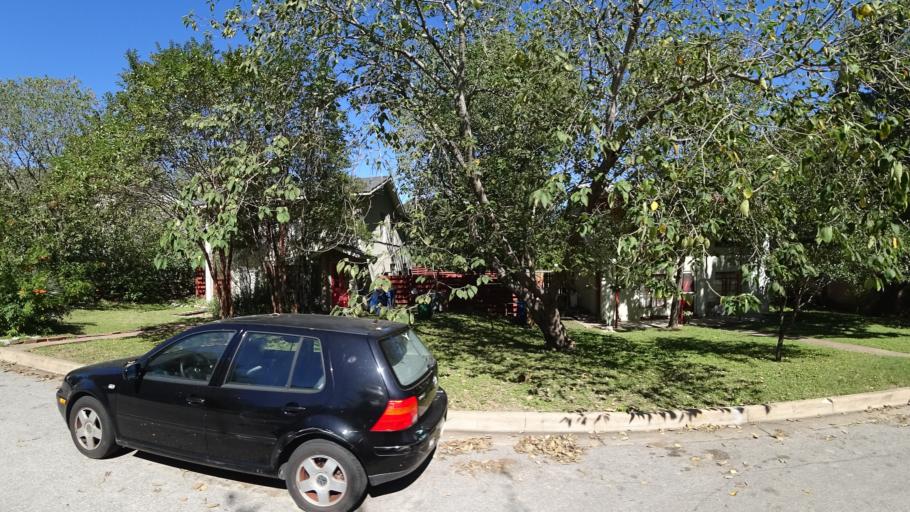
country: US
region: Texas
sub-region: Travis County
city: Austin
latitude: 30.2949
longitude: -97.7145
